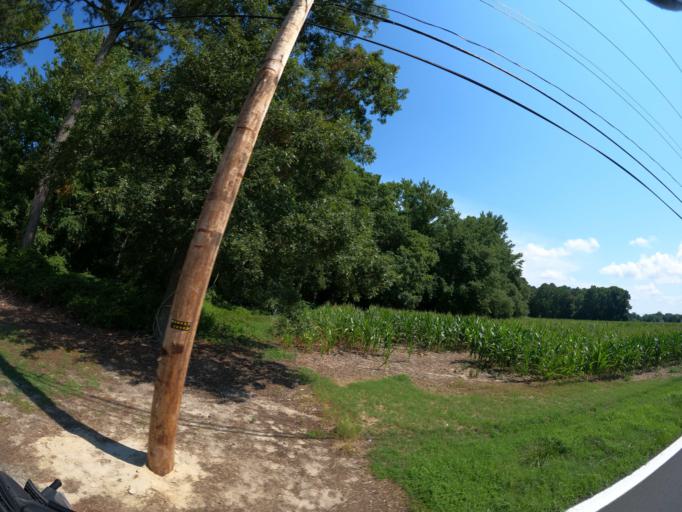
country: US
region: Delaware
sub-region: Sussex County
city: Selbyville
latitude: 38.4505
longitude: -75.1862
